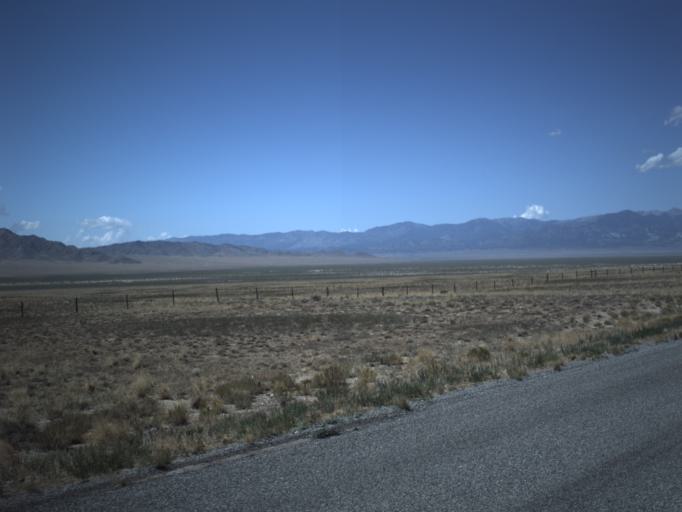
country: US
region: Nevada
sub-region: White Pine County
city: McGill
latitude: 39.0396
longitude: -113.8204
